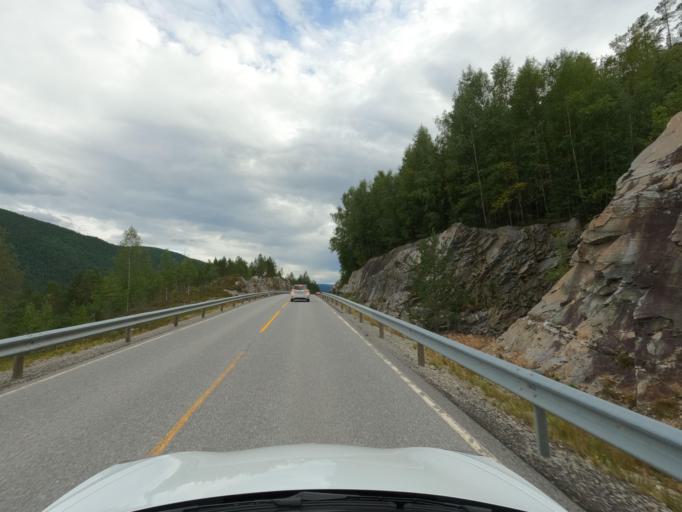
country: NO
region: Telemark
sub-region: Hjartdal
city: Sauland
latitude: 59.7651
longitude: 9.0186
